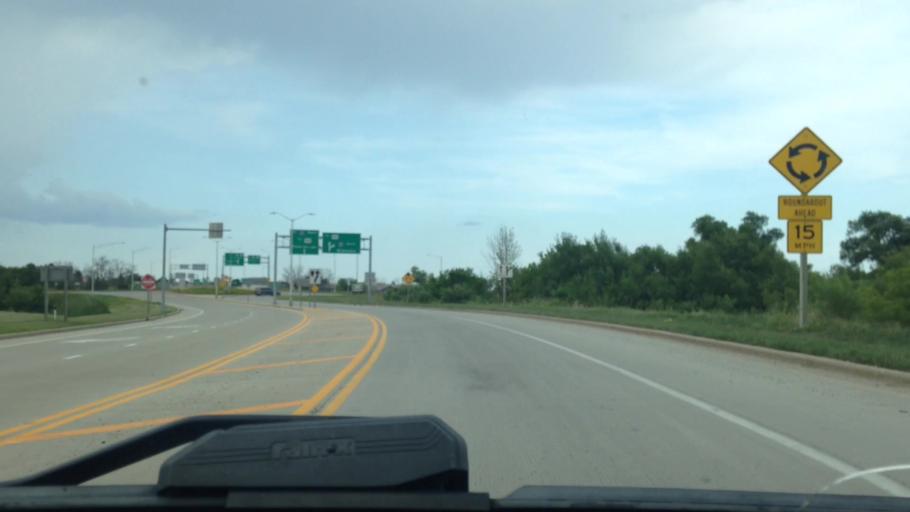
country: US
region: Wisconsin
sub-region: Washington County
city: Richfield
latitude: 43.2809
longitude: -88.1978
